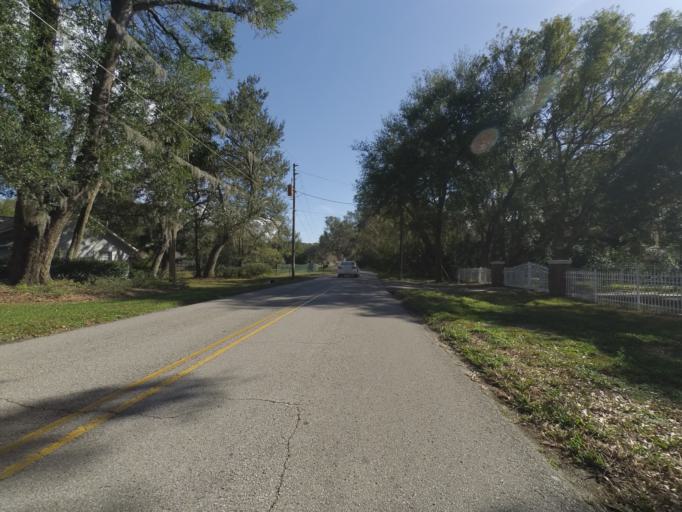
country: US
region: Florida
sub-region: Lake County
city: Mount Dora
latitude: 28.8180
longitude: -81.6508
